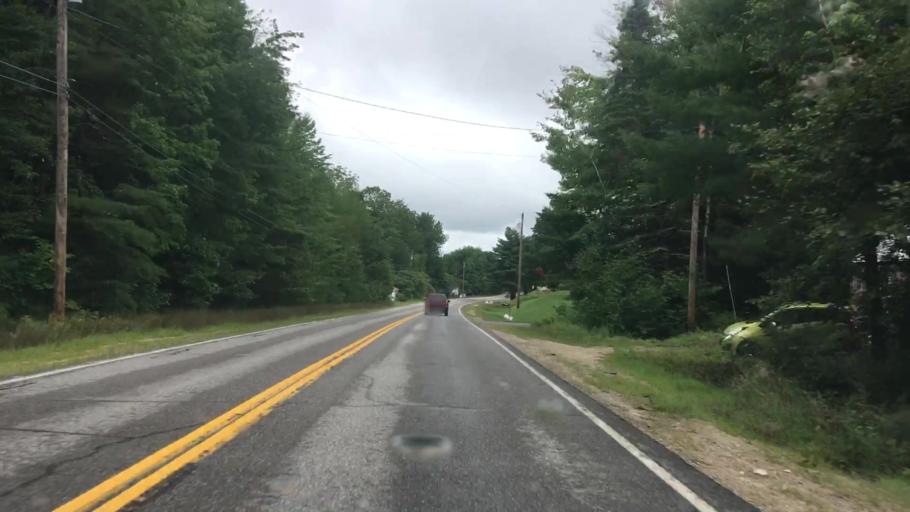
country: US
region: Maine
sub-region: Oxford County
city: Brownfield
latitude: 43.9636
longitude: -70.9070
